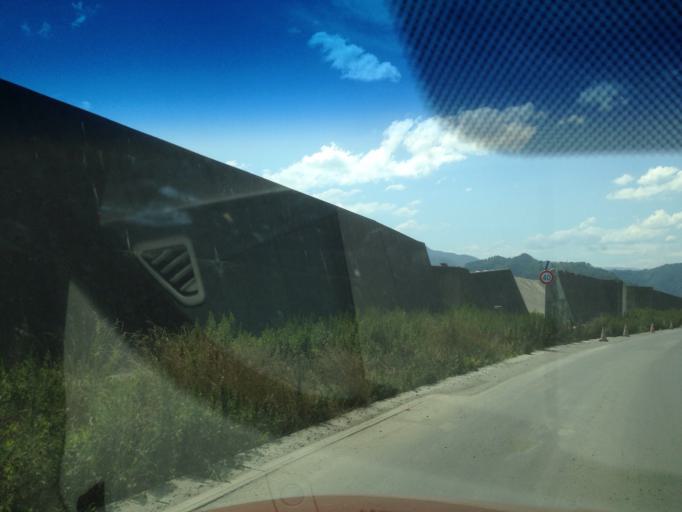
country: JP
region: Iwate
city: Otsuchi
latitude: 39.3557
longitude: 141.9210
